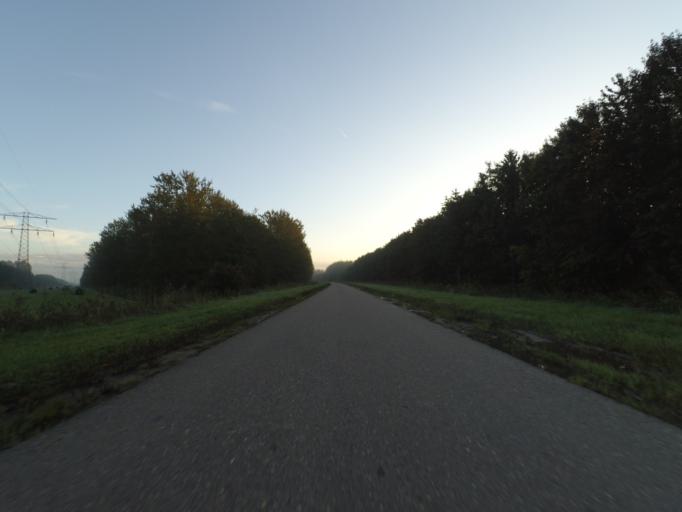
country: NL
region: Flevoland
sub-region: Gemeente Zeewolde
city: Zeewolde
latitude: 52.3314
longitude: 5.4544
